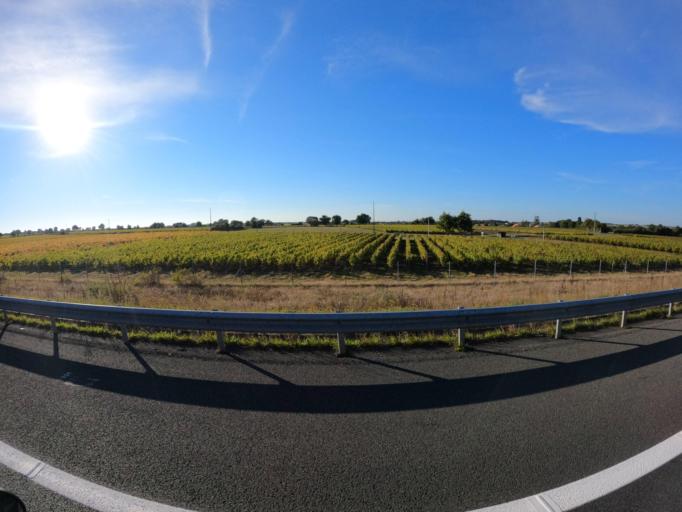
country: FR
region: Pays de la Loire
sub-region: Departement de Maine-et-Loire
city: Saint-Lambert-du-Lattay
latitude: 47.2912
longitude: -0.6140
